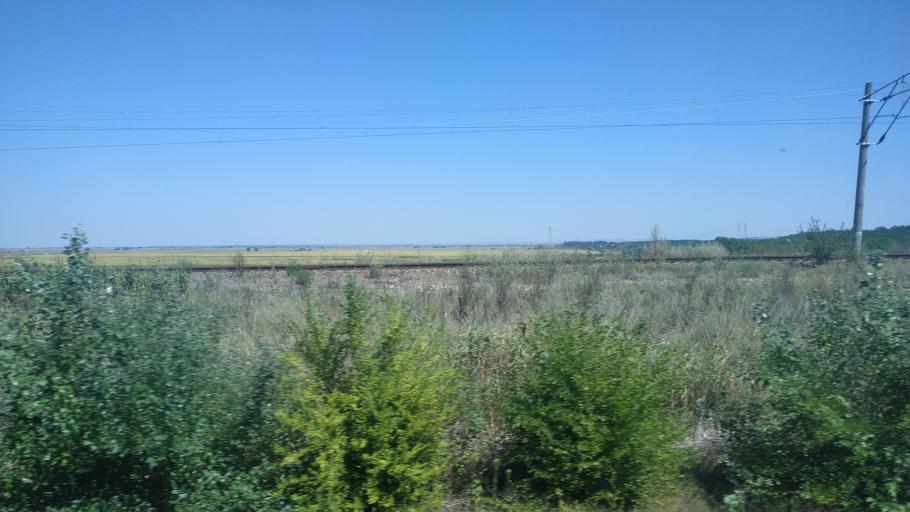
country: RO
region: Constanta
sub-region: Oras Cernavoda
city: Cernavoda
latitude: 44.3445
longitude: 27.9994
